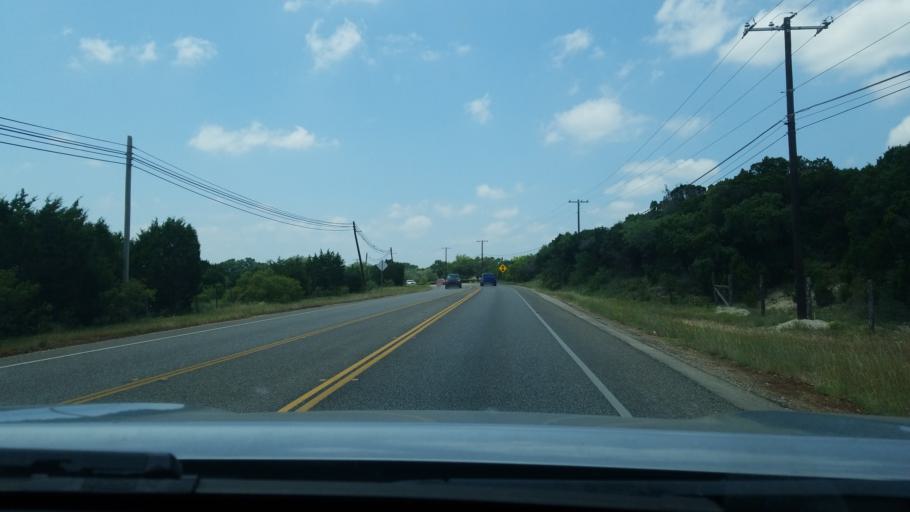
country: US
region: Texas
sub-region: Hays County
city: Woodcreek
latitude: 30.0199
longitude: -98.1319
